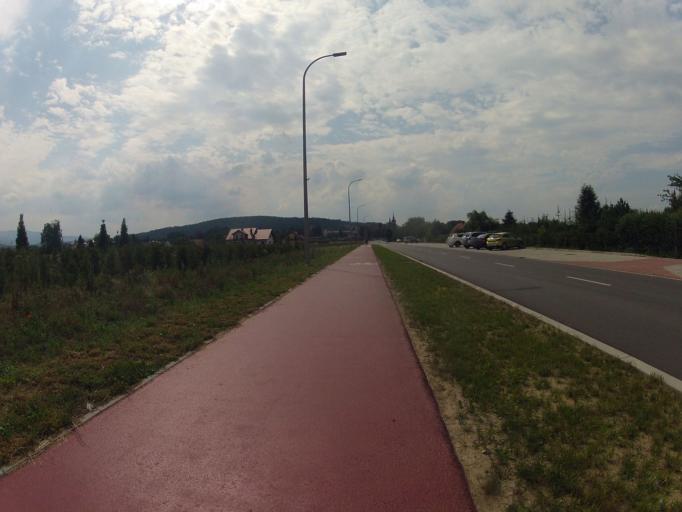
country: PL
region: Lesser Poland Voivodeship
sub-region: Powiat nowosadecki
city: Stary Sacz
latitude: 49.5616
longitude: 20.6482
